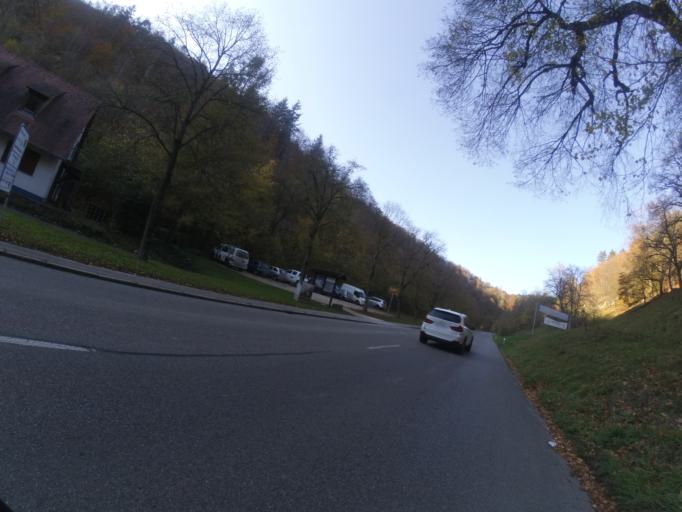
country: DE
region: Baden-Wuerttemberg
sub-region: Tuebingen Region
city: Blaubeuren
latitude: 48.4145
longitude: 9.7788
